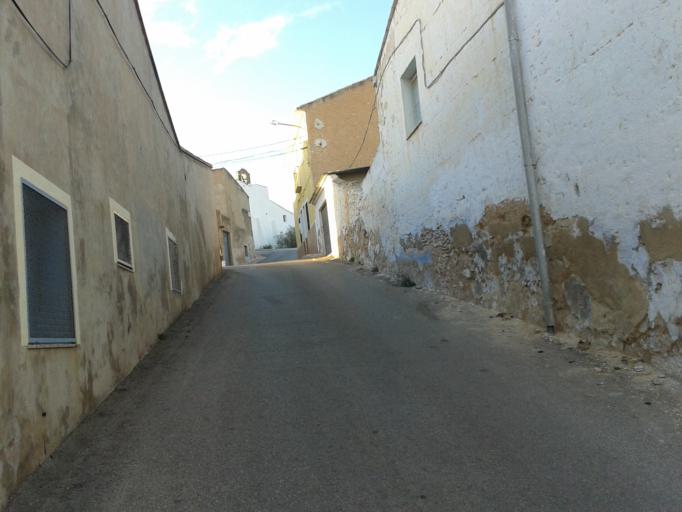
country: ES
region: Castille-La Mancha
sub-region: Provincia de Albacete
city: Caudete
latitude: 38.7045
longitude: -0.9908
